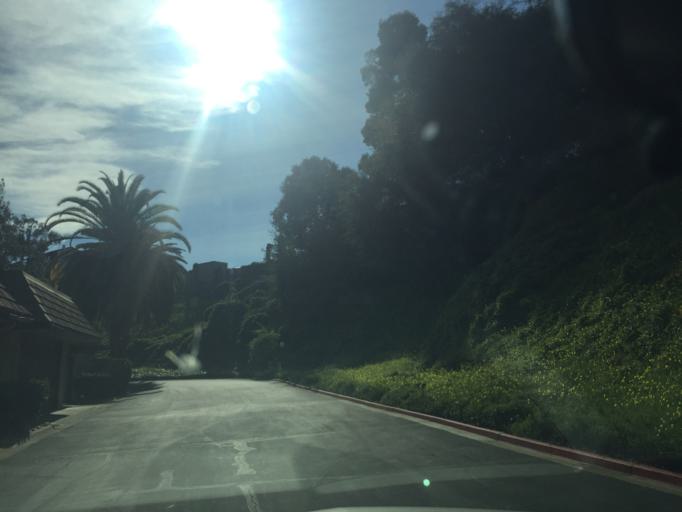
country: US
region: California
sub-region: San Diego County
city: Lemon Grove
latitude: 32.7616
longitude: -117.0838
